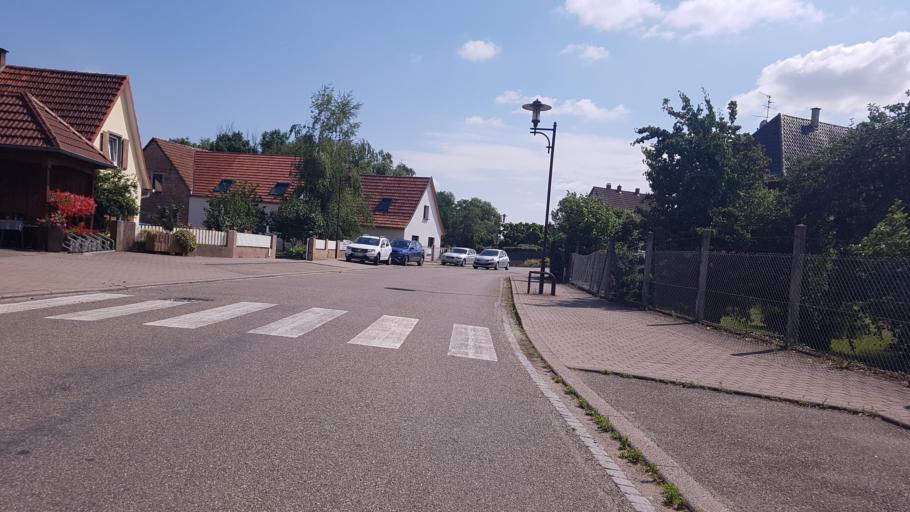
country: FR
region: Alsace
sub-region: Departement du Bas-Rhin
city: Herrlisheim
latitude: 48.7146
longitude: 7.9152
